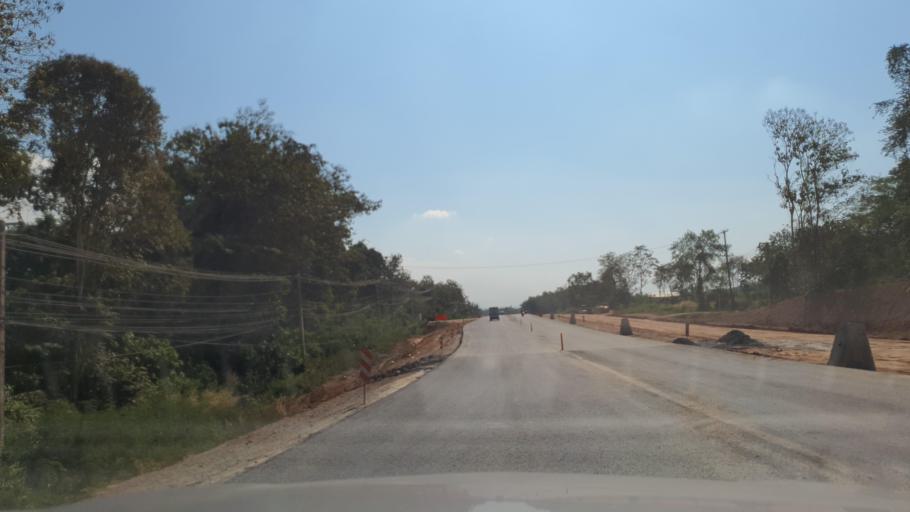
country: TH
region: Nan
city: Nan
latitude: 18.8241
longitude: 100.7661
